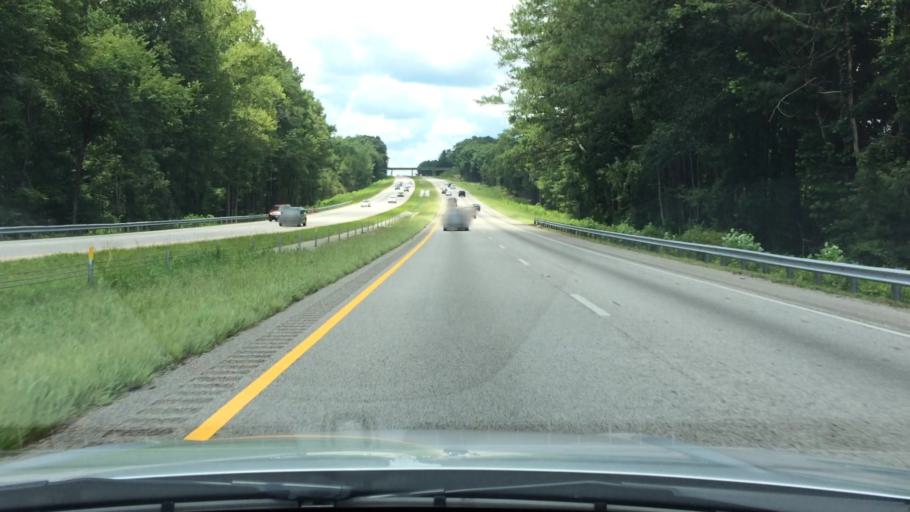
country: US
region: South Carolina
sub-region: Laurens County
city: Joanna
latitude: 34.4754
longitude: -81.8151
